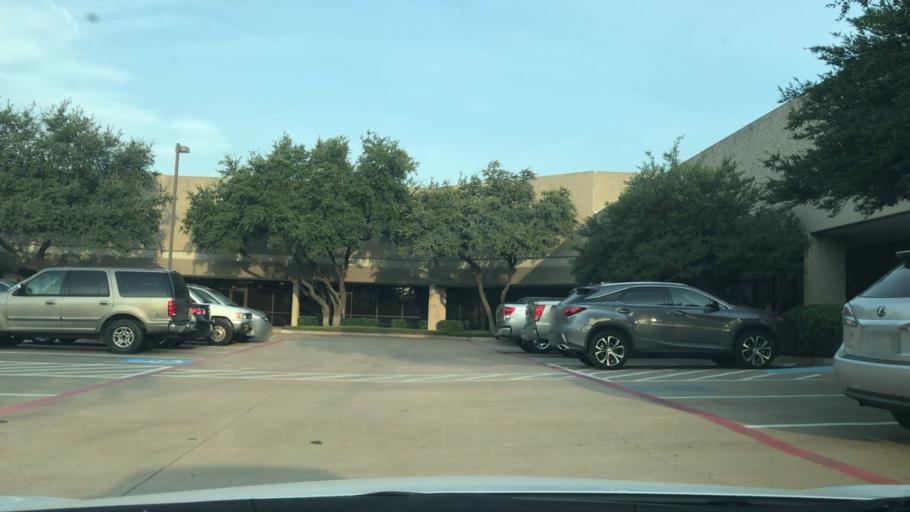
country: US
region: Texas
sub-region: Dallas County
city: Farmers Branch
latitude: 32.8978
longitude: -96.9082
